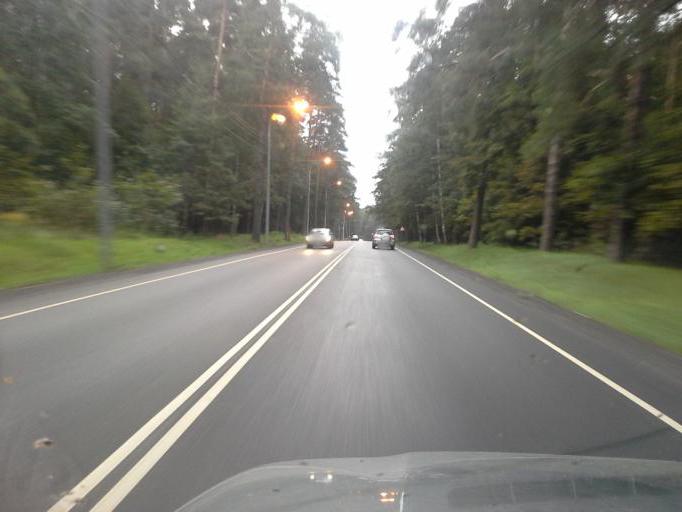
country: RU
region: Moskovskaya
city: Nikolina Gora
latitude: 55.7098
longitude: 37.0612
